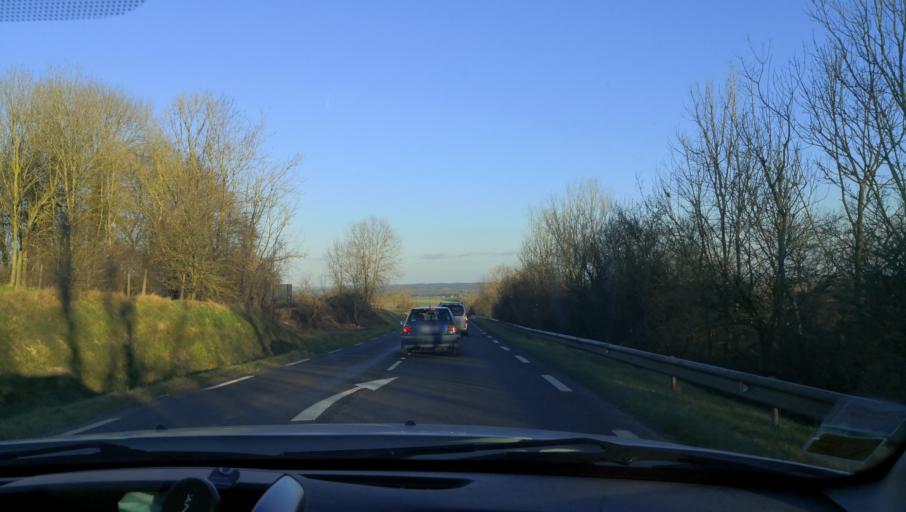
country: FR
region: Haute-Normandie
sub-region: Departement de la Seine-Maritime
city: Buchy
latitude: 49.5935
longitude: 1.4459
